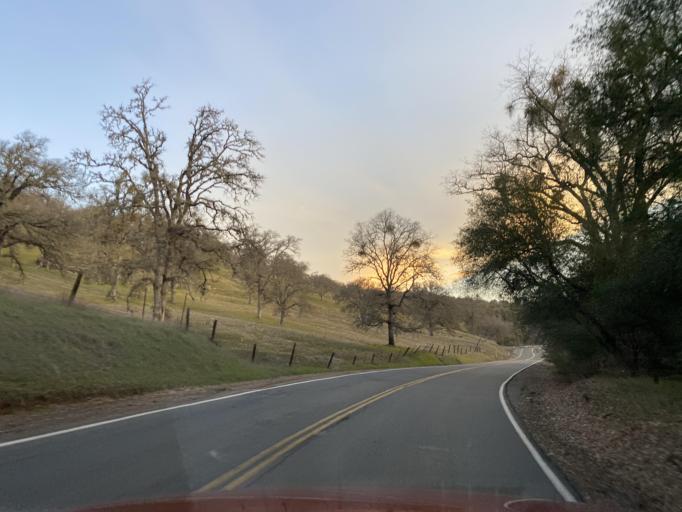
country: US
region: California
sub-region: Amador County
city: Plymouth
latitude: 38.4991
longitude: -120.7880
